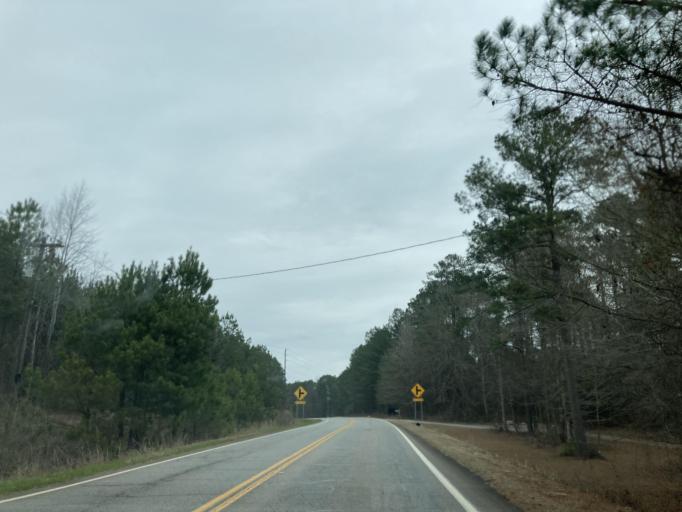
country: US
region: Georgia
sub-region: Jones County
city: Gray
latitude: 32.9753
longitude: -83.6134
